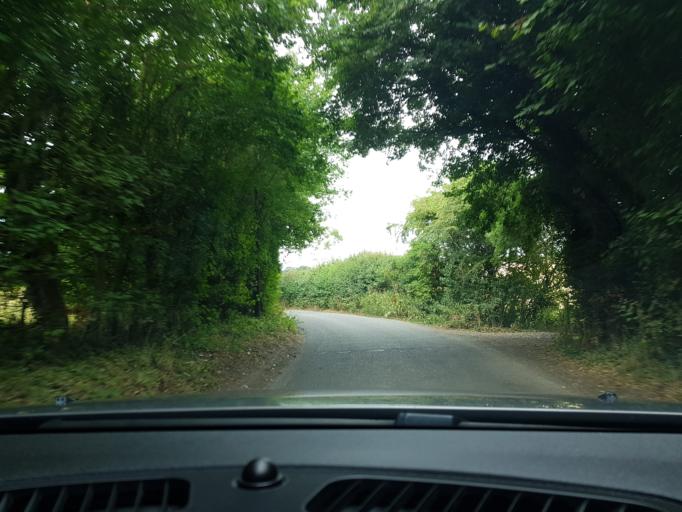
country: GB
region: England
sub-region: West Berkshire
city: Hungerford
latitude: 51.4378
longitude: -1.4806
